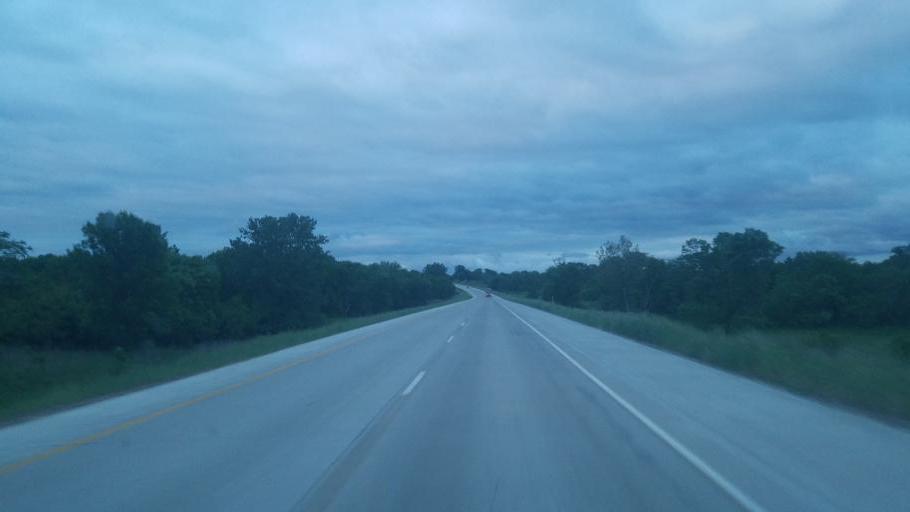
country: US
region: Iowa
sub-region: Decatur County
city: Lamoni
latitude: 40.5950
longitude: -93.9153
